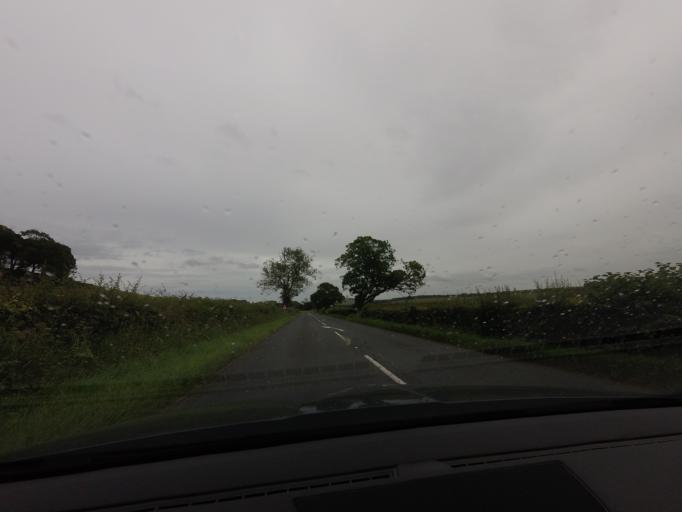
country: GB
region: Scotland
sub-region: Moray
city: Cullen
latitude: 57.6788
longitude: -2.7981
